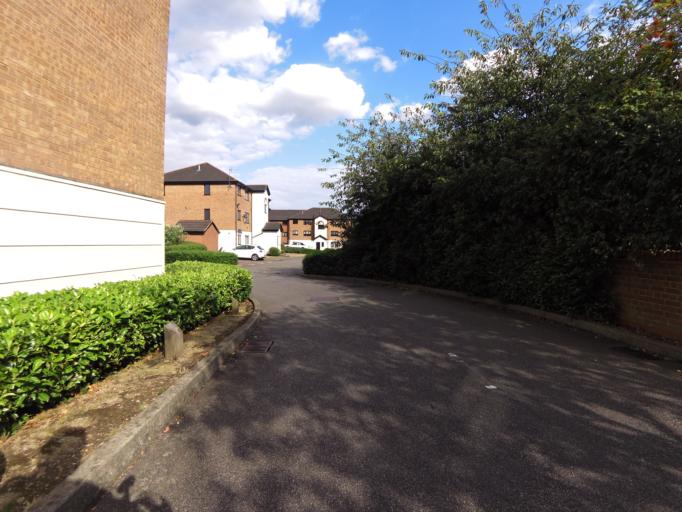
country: GB
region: England
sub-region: Hertfordshire
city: Hoddesdon
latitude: 51.7635
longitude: -0.0077
